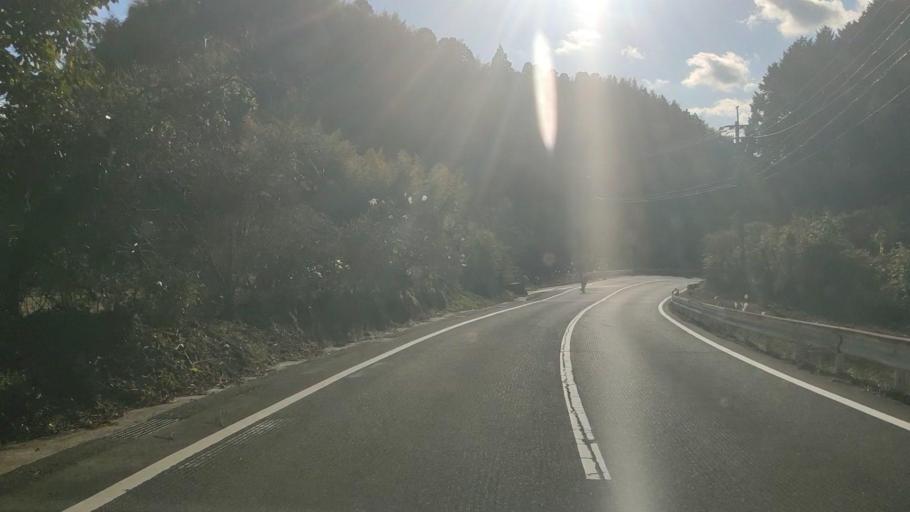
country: JP
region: Saga Prefecture
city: Kanzakimachi-kanzaki
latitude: 33.3935
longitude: 130.2707
